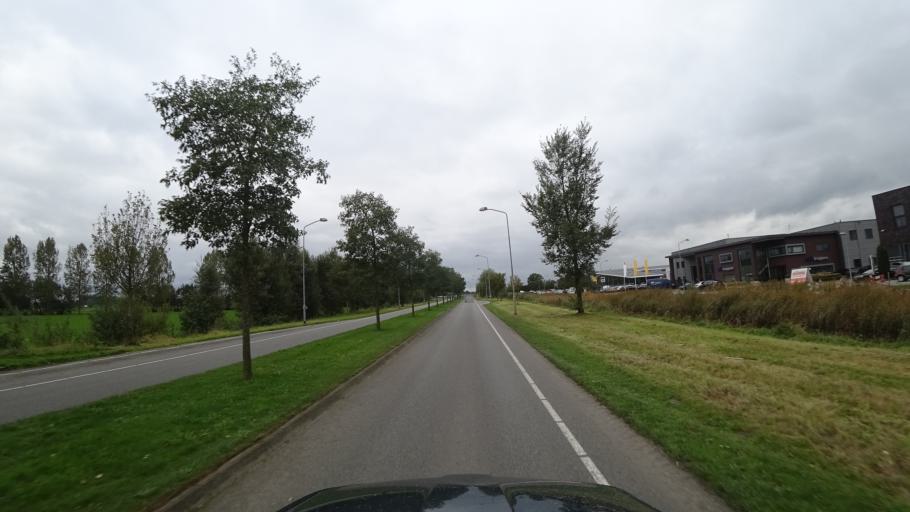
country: NL
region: Gelderland
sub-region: Gemeente Nijkerk
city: Nijkerk
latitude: 52.2278
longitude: 5.4616
